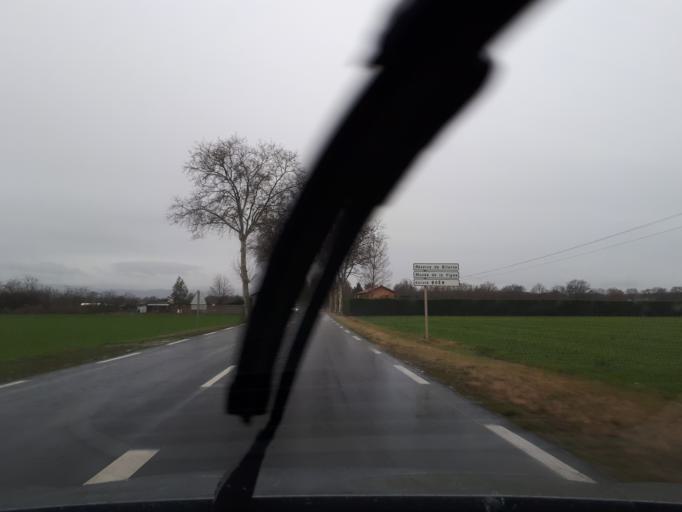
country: FR
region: Rhone-Alpes
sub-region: Departement de la Loire
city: Feurs
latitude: 45.7377
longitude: 4.1680
